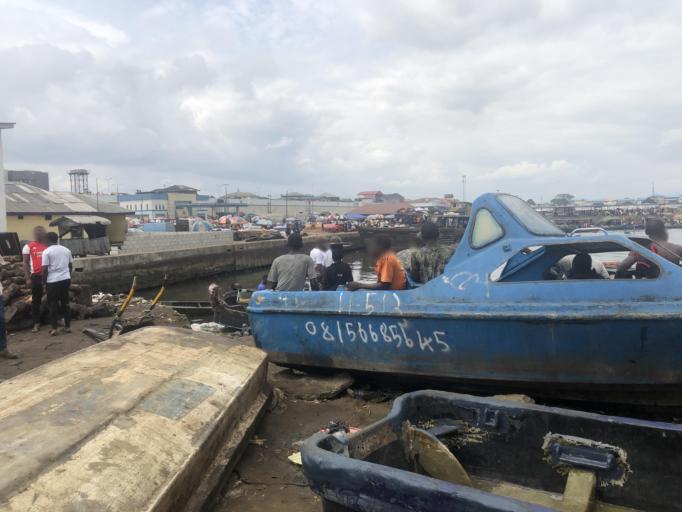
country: NG
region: Rivers
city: Port Harcourt
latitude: 4.7570
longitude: 7.0226
